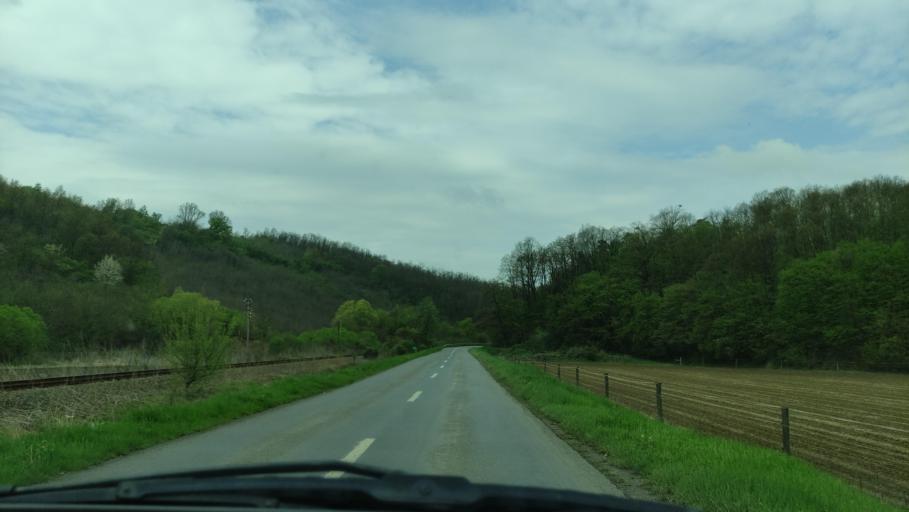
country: HU
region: Baranya
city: Komlo
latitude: 46.2248
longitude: 18.2260
